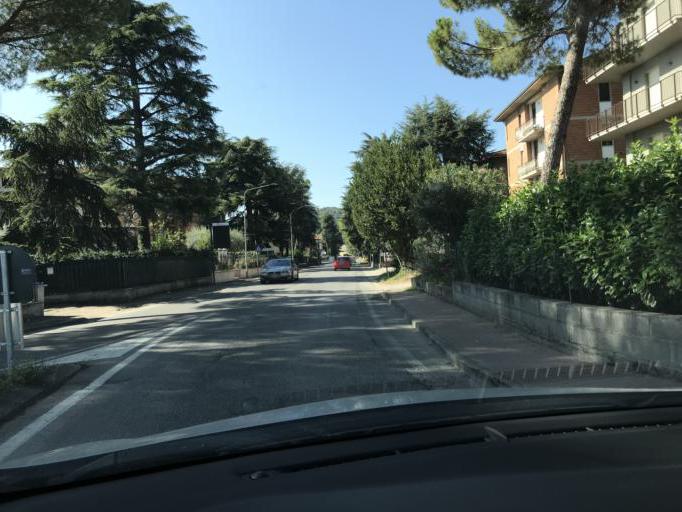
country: IT
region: Umbria
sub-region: Provincia di Perugia
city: Ponte Felcino
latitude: 43.1129
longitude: 12.4511
